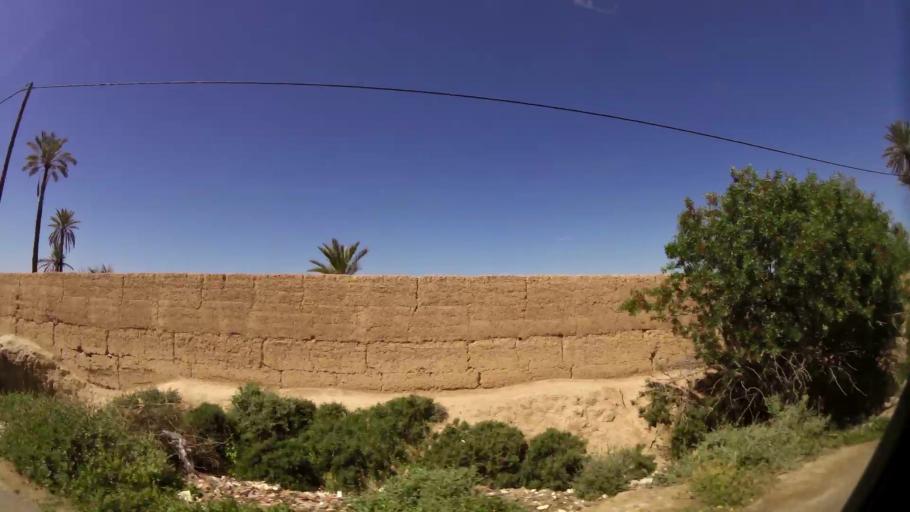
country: MA
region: Marrakech-Tensift-Al Haouz
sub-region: Marrakech
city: Marrakesh
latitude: 31.6712
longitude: -7.9796
